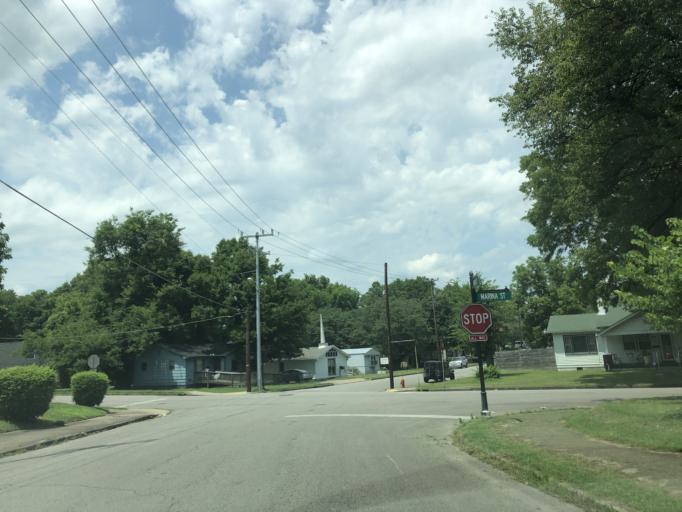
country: US
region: Tennessee
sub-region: Davidson County
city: Nashville
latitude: 36.1803
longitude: -86.7586
